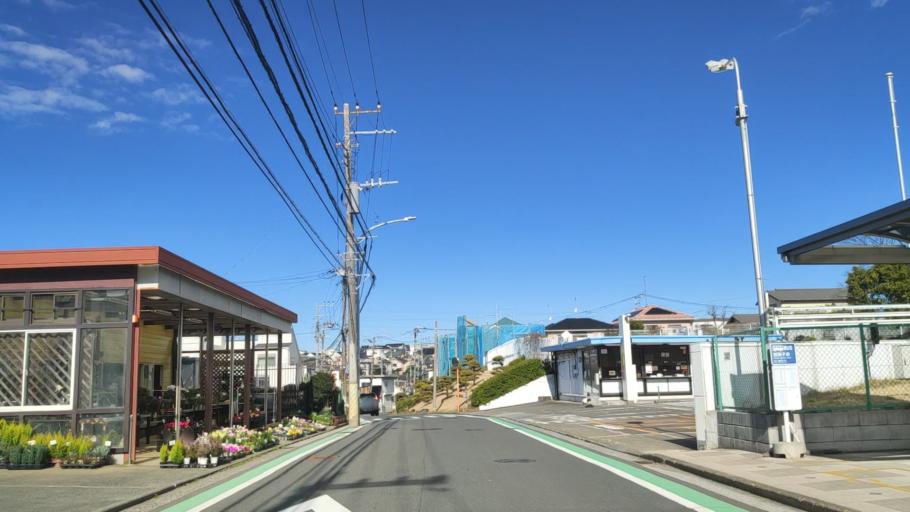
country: JP
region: Kanagawa
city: Yokohama
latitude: 35.4867
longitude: 139.5752
